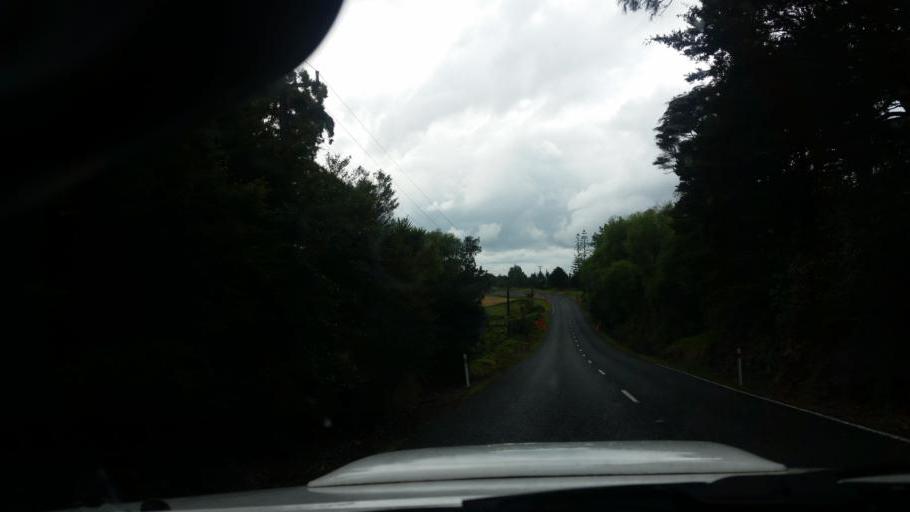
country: NZ
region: Auckland
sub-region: Auckland
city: Wellsford
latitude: -36.1479
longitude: 174.2220
